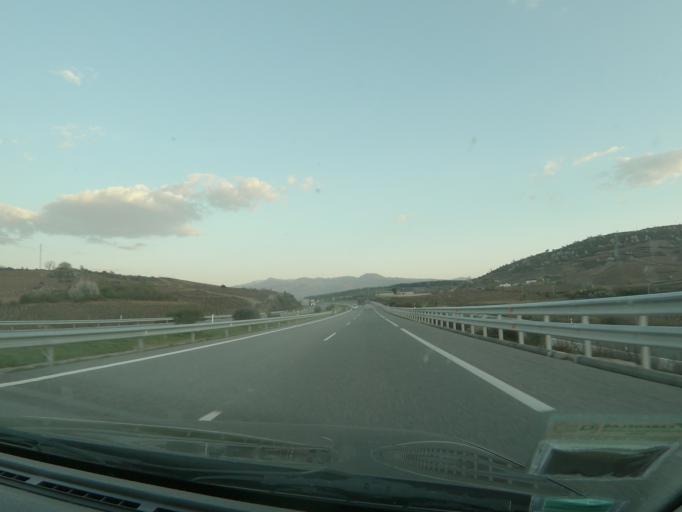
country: ES
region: Castille and Leon
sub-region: Provincia de Leon
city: Villadecanes
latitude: 42.5805
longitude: -6.7827
